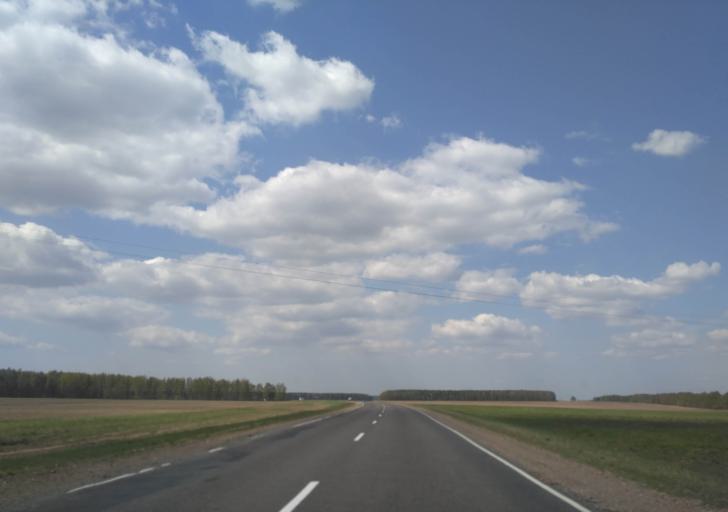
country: BY
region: Minsk
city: Vilyeyka
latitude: 54.5153
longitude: 27.0402
